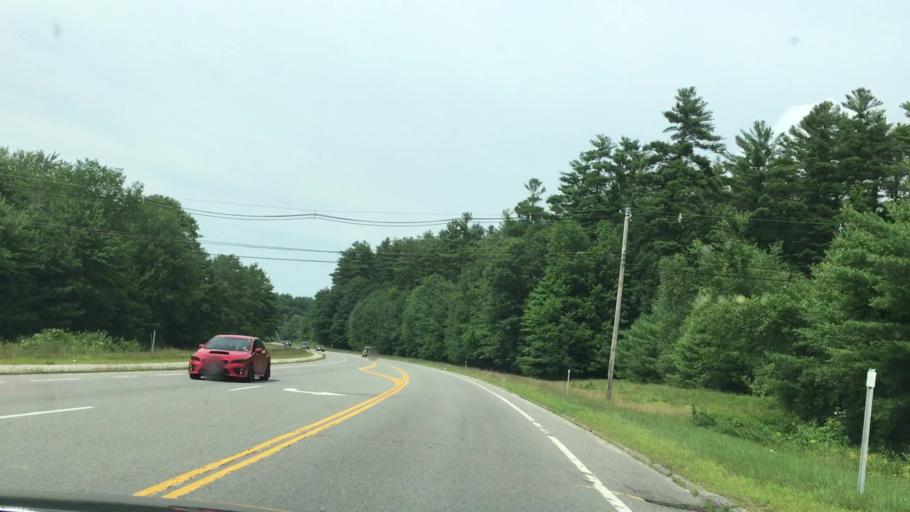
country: US
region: New Hampshire
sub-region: Hillsborough County
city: Peterborough
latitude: 42.8926
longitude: -71.9432
